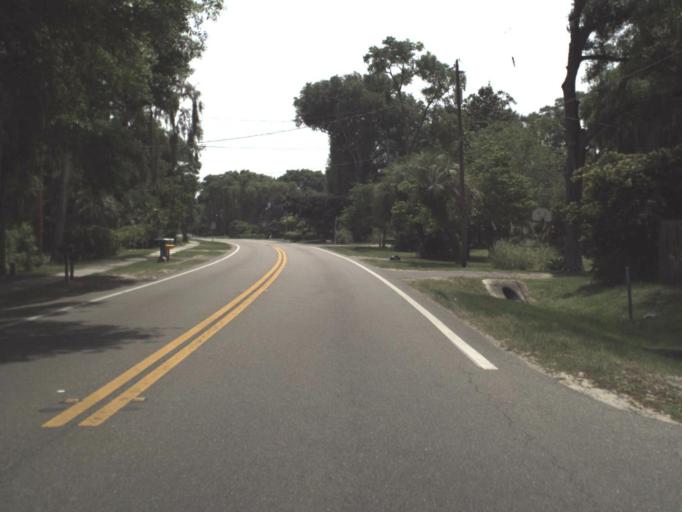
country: US
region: Florida
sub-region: Clay County
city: Keystone Heights
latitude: 29.7765
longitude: -82.0338
